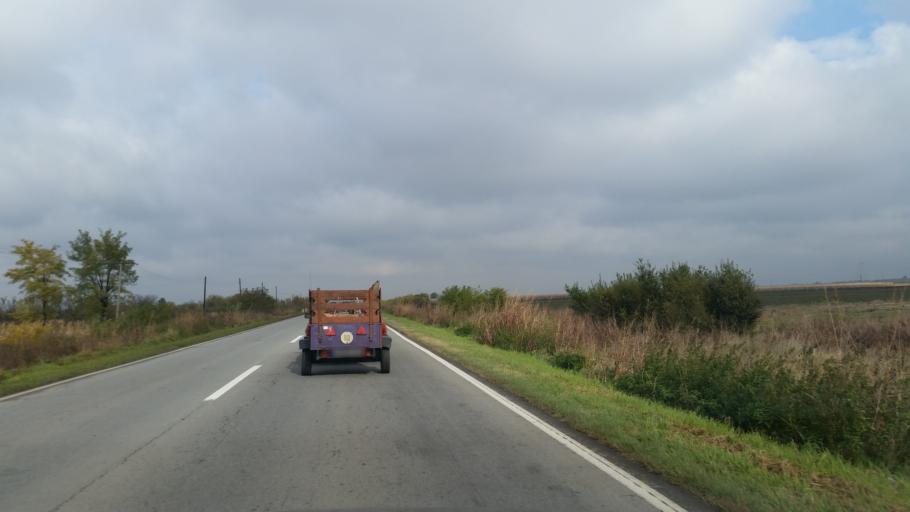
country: RS
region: Autonomna Pokrajina Vojvodina
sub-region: Srednjebanatski Okrug
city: Zrenjanin
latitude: 45.4233
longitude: 20.3709
